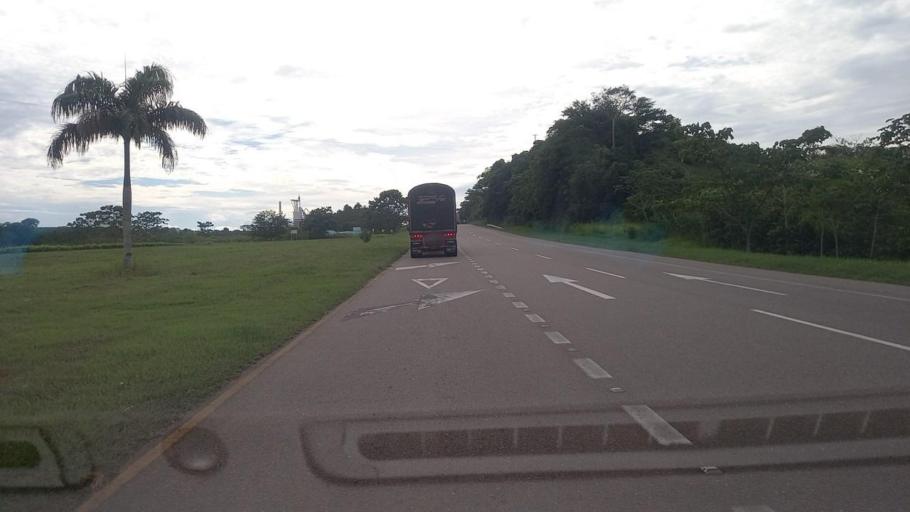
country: CO
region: Antioquia
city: Puerto Berrio
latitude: 6.3767
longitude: -74.4003
